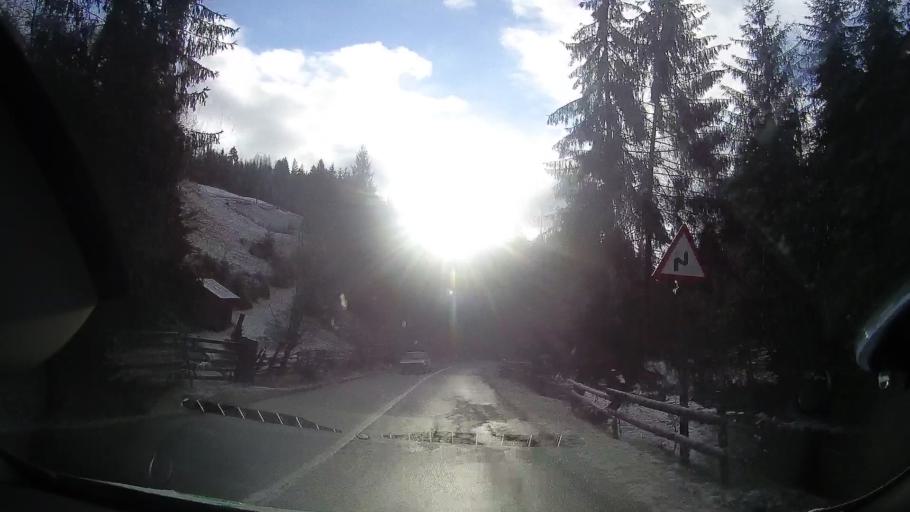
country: RO
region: Alba
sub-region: Comuna Horea
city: Horea
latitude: 46.4849
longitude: 22.9617
